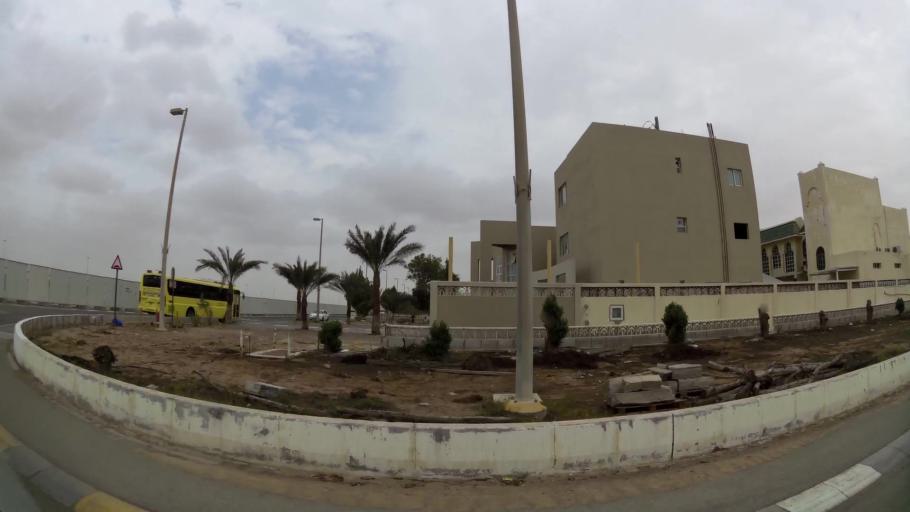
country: AE
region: Abu Dhabi
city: Abu Dhabi
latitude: 24.3299
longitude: 54.6331
